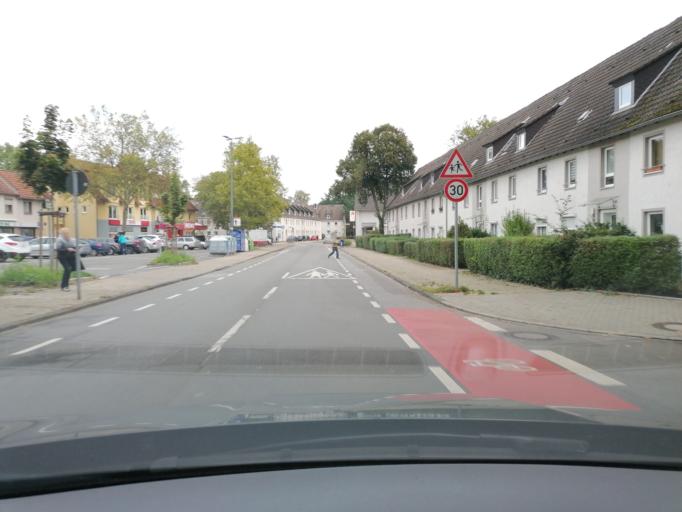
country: DE
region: North Rhine-Westphalia
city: Herten
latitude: 51.5632
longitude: 7.1089
